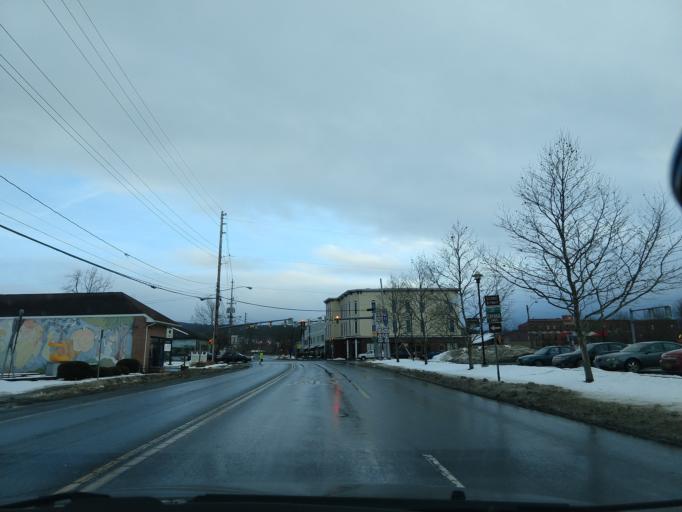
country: US
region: New York
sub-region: Tompkins County
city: Ithaca
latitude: 42.4416
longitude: -76.5125
